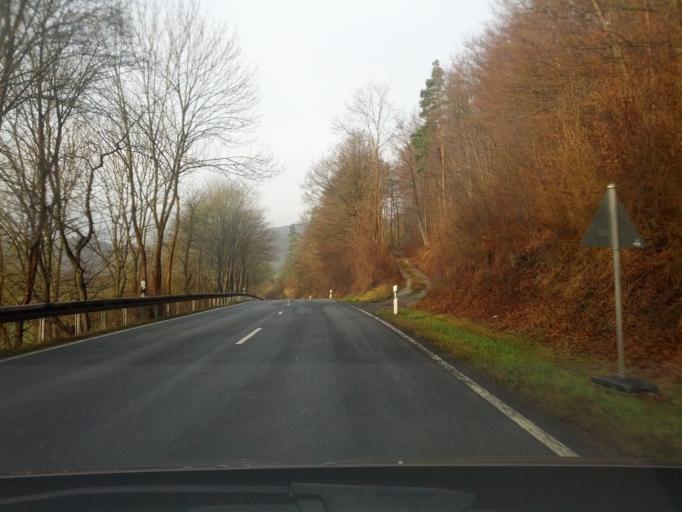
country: DE
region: Hesse
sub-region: Regierungsbezirk Kassel
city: Eschwege
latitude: 51.1190
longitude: 10.0154
